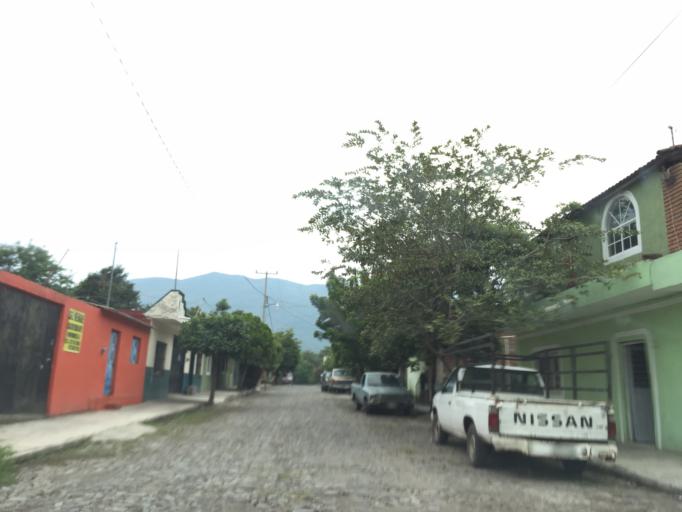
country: MX
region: Colima
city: Comala
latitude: 19.3714
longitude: -103.7992
